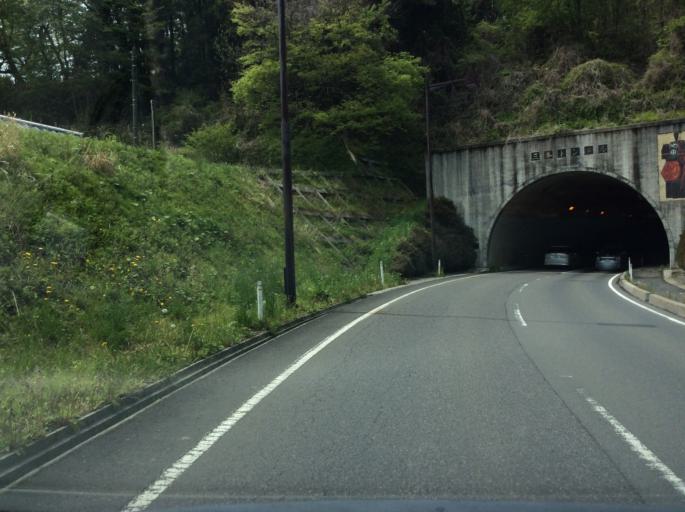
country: JP
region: Fukushima
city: Miharu
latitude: 37.3968
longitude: 140.4779
